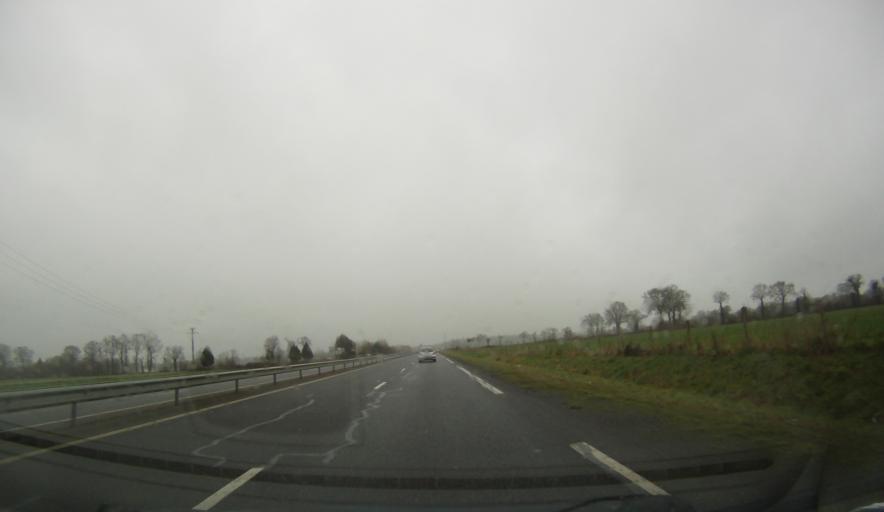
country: FR
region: Brittany
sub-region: Departement d'Ille-et-Vilaine
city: Saint-Armel
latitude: 48.0216
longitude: -1.6013
